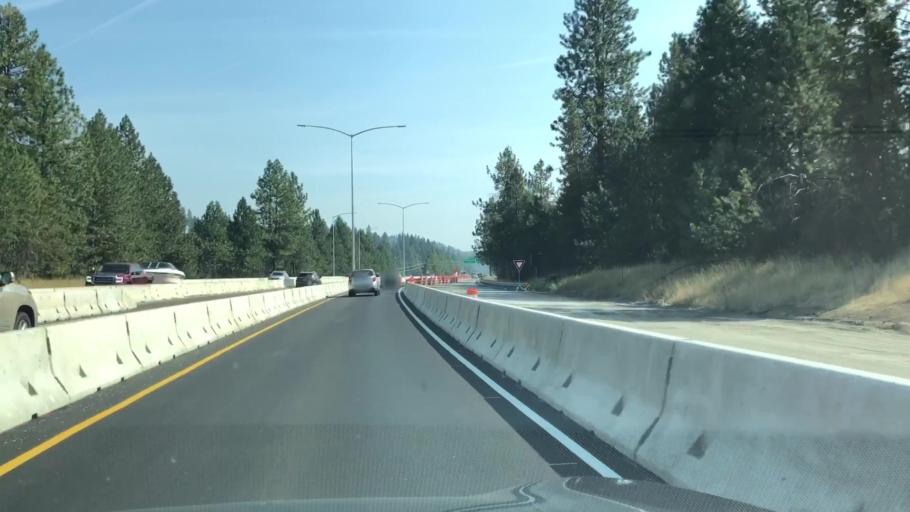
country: US
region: Idaho
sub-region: Kootenai County
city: Coeur d'Alene
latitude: 47.6939
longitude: -116.7703
